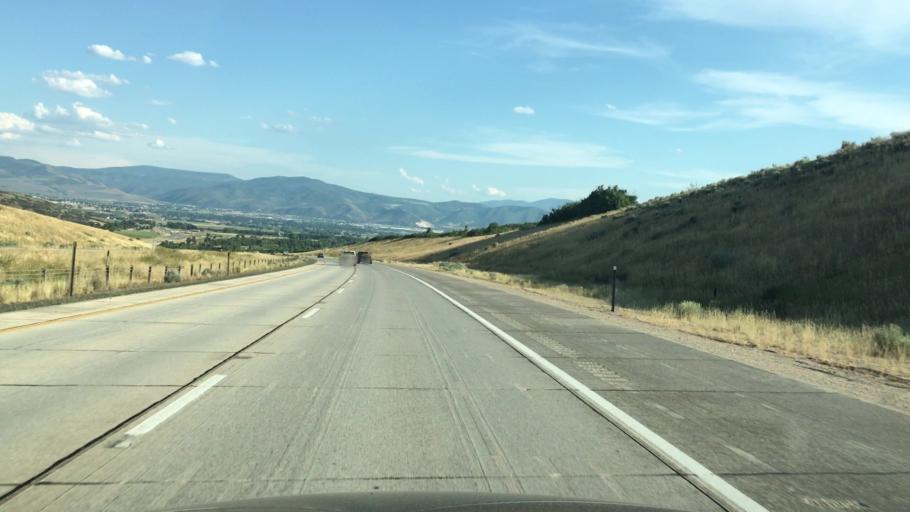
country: US
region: Utah
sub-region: Wasatch County
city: Heber
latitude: 40.5800
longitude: -111.4364
